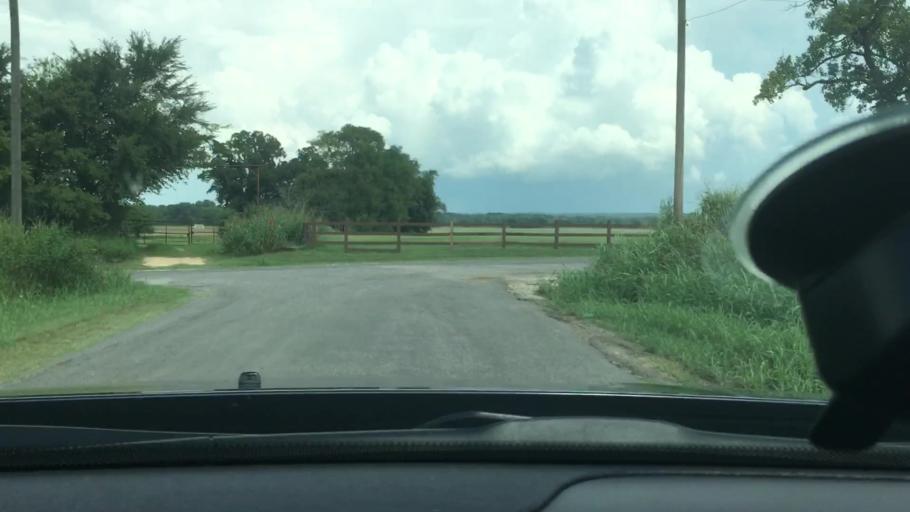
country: US
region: Oklahoma
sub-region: Carter County
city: Dickson
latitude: 34.2268
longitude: -96.8982
